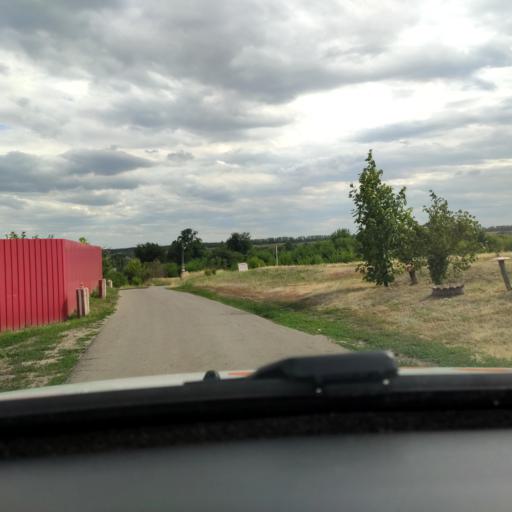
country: RU
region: Voronezj
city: Orlovo
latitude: 51.6519
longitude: 39.5712
